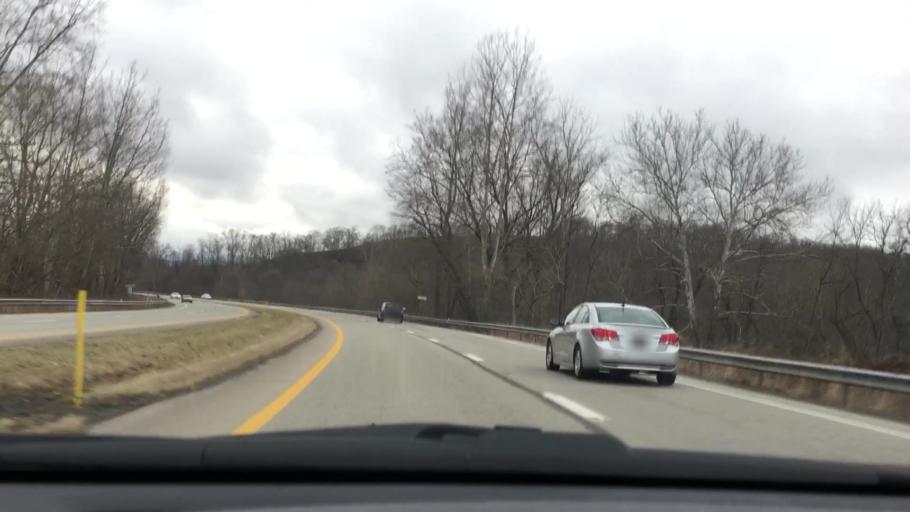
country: US
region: Pennsylvania
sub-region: Fayette County
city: Oliver
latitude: 39.9556
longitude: -79.7451
